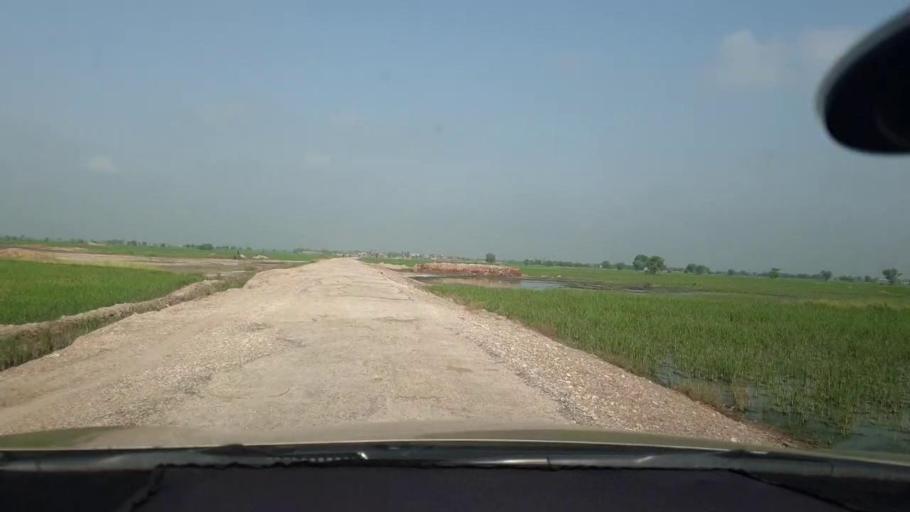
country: PK
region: Sindh
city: Kambar
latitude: 27.5373
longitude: 68.0578
